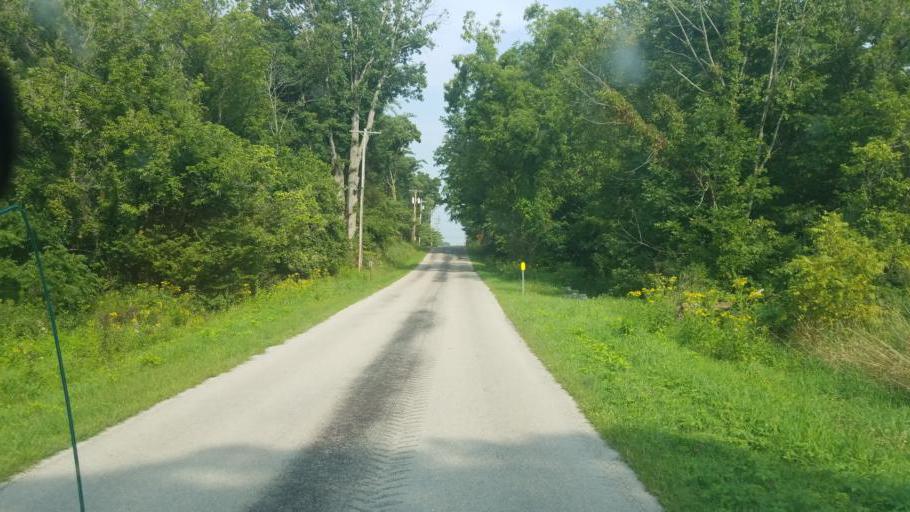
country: US
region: Ohio
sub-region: Lorain County
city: Wellington
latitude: 41.1294
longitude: -82.1262
